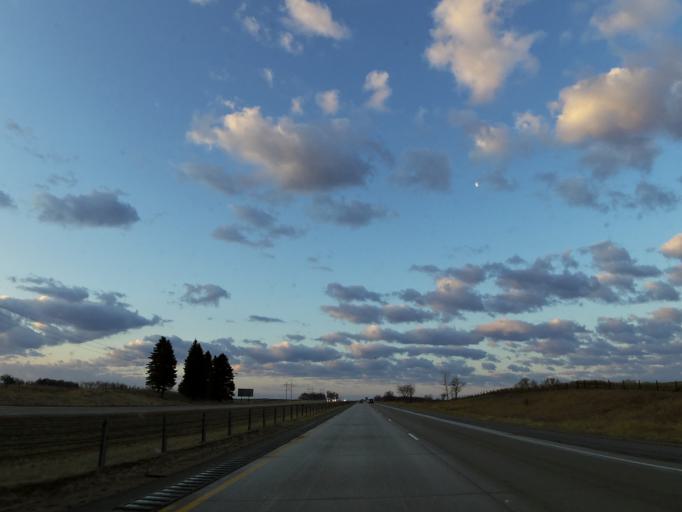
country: US
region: Minnesota
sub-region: Rice County
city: Dundas
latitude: 44.4454
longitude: -93.2926
